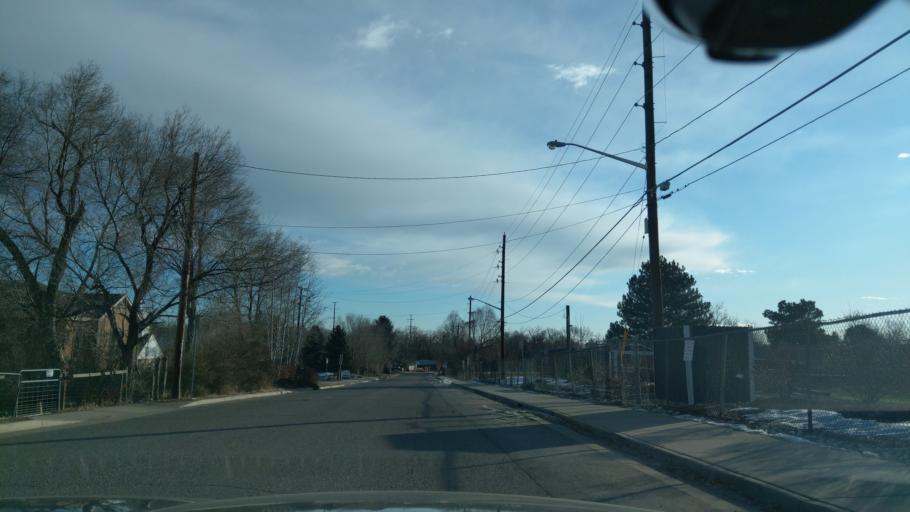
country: US
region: Colorado
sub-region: Jefferson County
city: Lakewood
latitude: 39.7310
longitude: -105.1070
